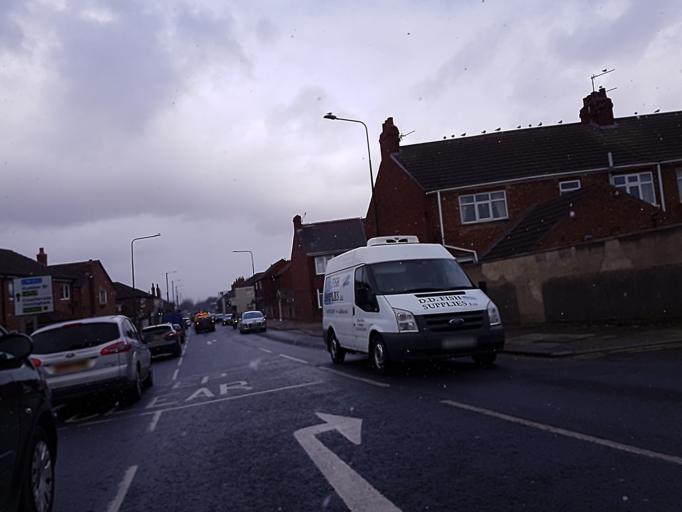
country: GB
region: England
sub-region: North East Lincolnshire
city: Grimbsy
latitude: 53.5712
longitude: -0.0982
